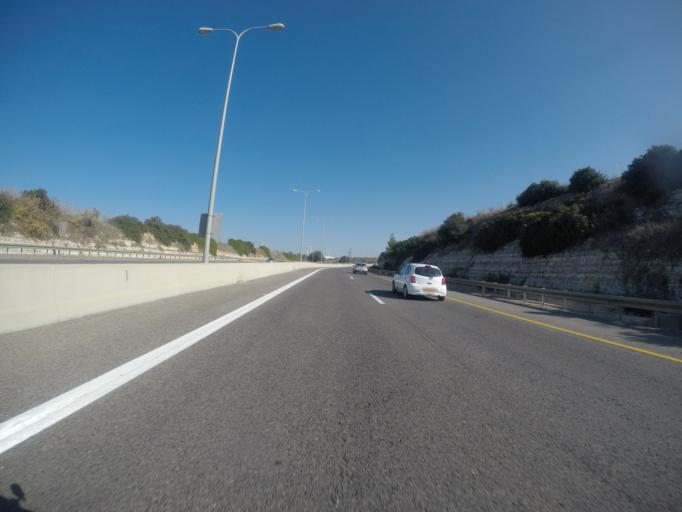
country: IL
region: Haifa
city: El Fureidis
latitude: 32.6087
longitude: 35.0338
